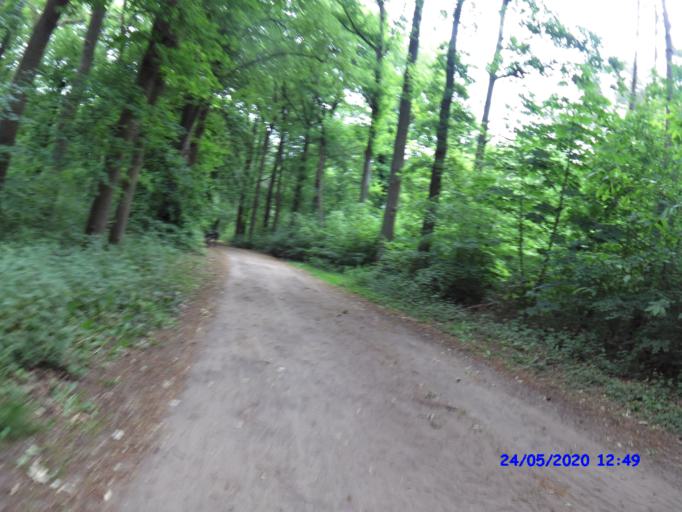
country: BE
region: Flanders
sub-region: Provincie Antwerpen
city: Retie
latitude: 51.2289
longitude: 5.0466
